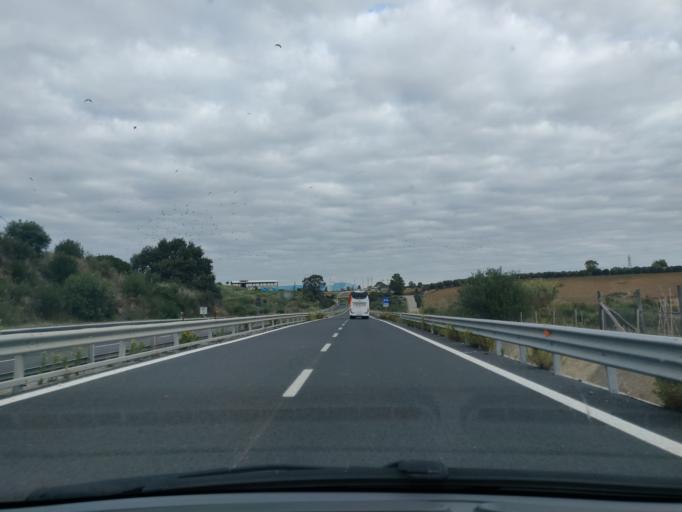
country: IT
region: Latium
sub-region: Citta metropolitana di Roma Capitale
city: Civitavecchia
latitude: 42.1160
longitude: 11.7921
